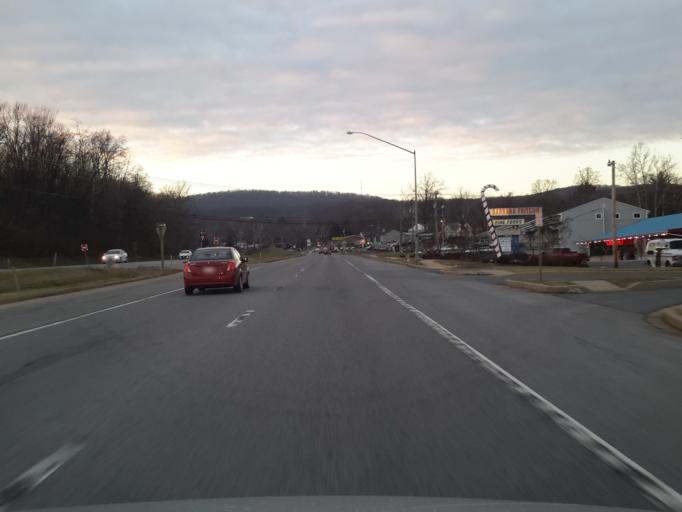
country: US
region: Maryland
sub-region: Frederick County
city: Braddock Heights
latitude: 39.4234
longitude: -77.4686
